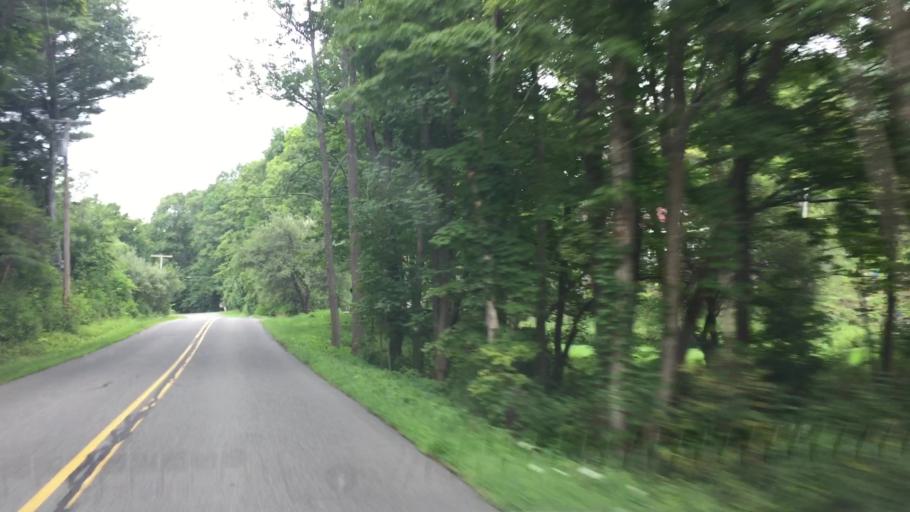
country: US
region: Massachusetts
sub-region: Berkshire County
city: Housatonic
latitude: 42.2556
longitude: -73.4084
